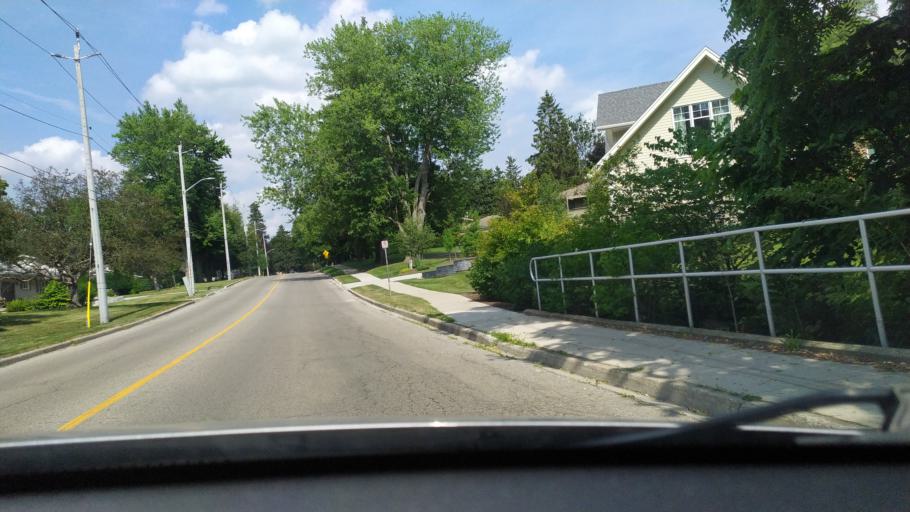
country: CA
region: Ontario
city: Stratford
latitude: 43.3782
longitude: -80.9761
